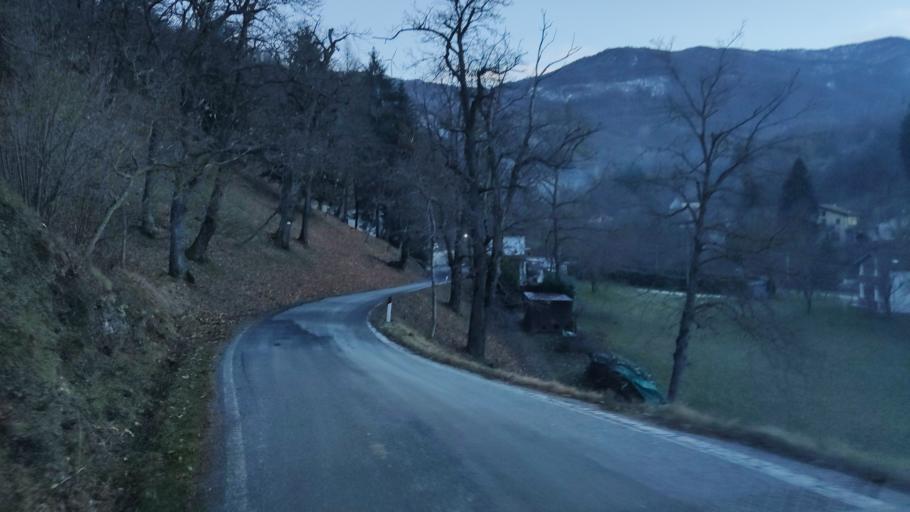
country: IT
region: Piedmont
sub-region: Provincia di Cuneo
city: Viola
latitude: 44.2884
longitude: 7.9784
